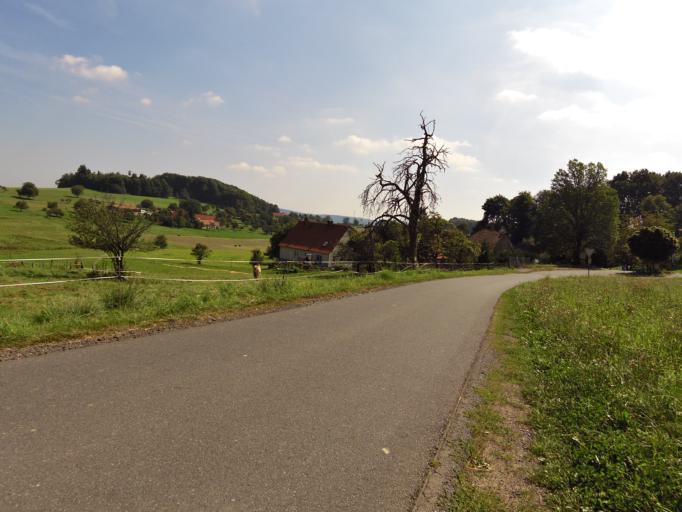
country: DE
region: Hesse
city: Reichelsheim
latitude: 49.7205
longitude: 8.8006
